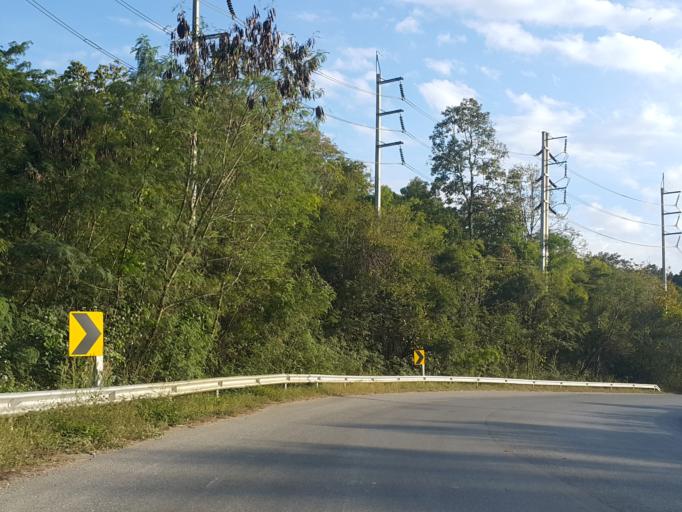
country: TH
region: Lampang
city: Chae Hom
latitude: 18.5232
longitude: 99.5572
